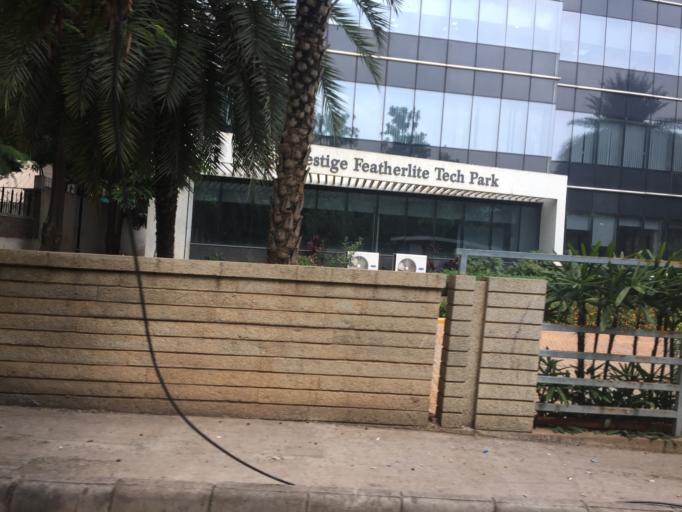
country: IN
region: Karnataka
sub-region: Bangalore Rural
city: Hoskote
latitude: 12.9812
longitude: 77.7219
